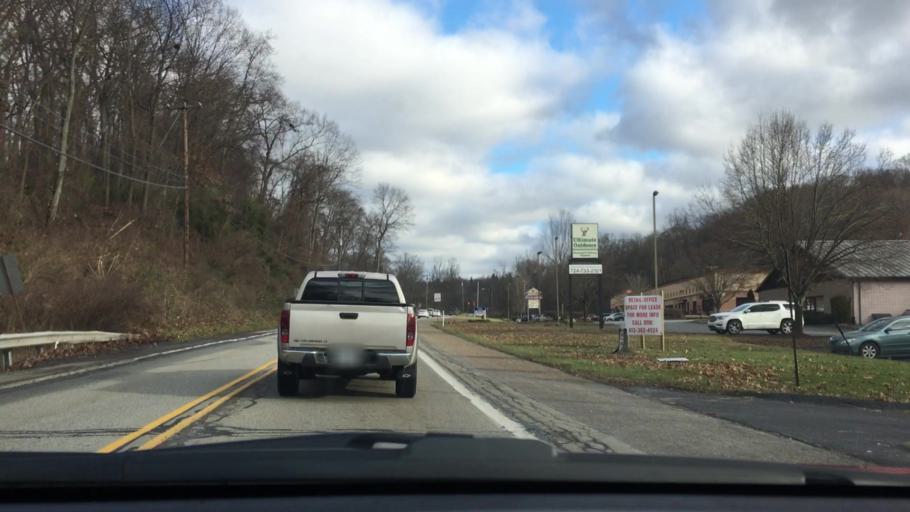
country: US
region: Pennsylvania
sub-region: Allegheny County
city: Plum
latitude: 40.4784
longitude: -79.7066
